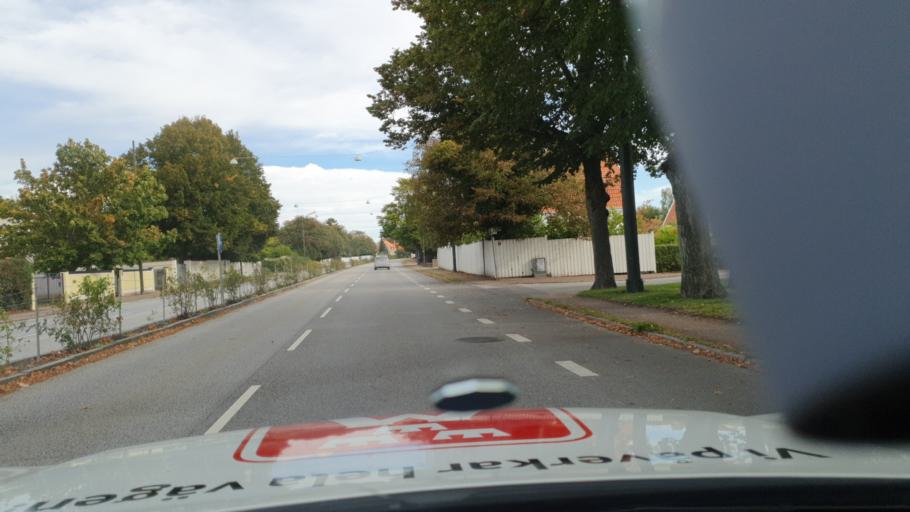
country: SE
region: Skane
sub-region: Malmo
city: Bunkeflostrand
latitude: 55.5849
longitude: 12.9498
